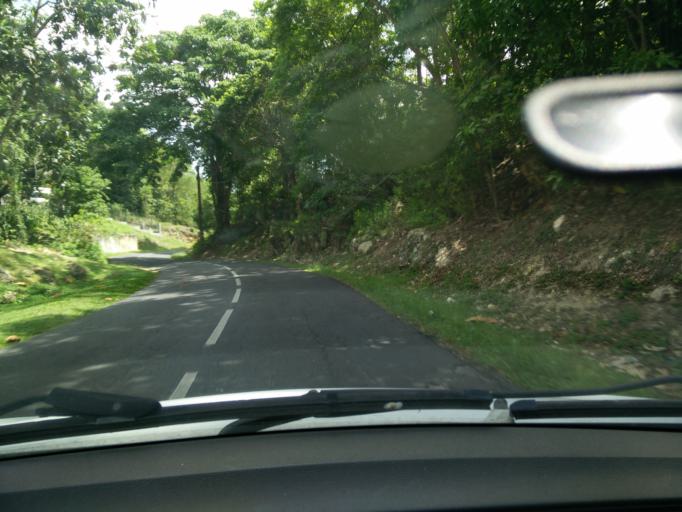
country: GP
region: Guadeloupe
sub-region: Guadeloupe
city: Les Abymes
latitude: 16.2921
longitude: -61.4572
